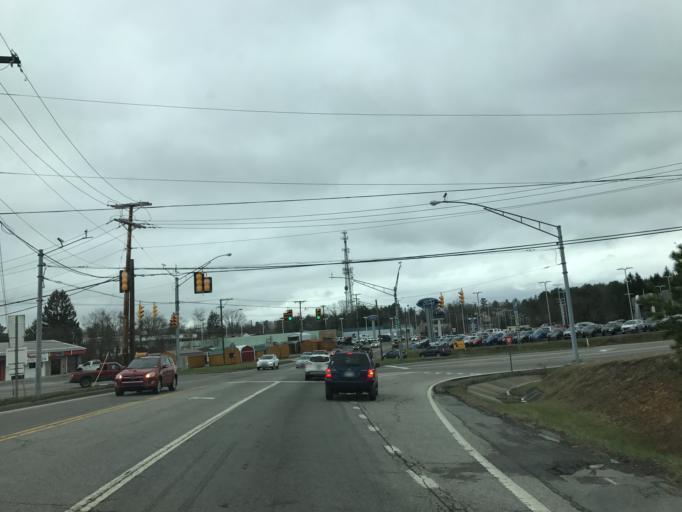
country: US
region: West Virginia
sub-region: Raleigh County
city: Beckley
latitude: 37.7938
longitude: -81.1731
